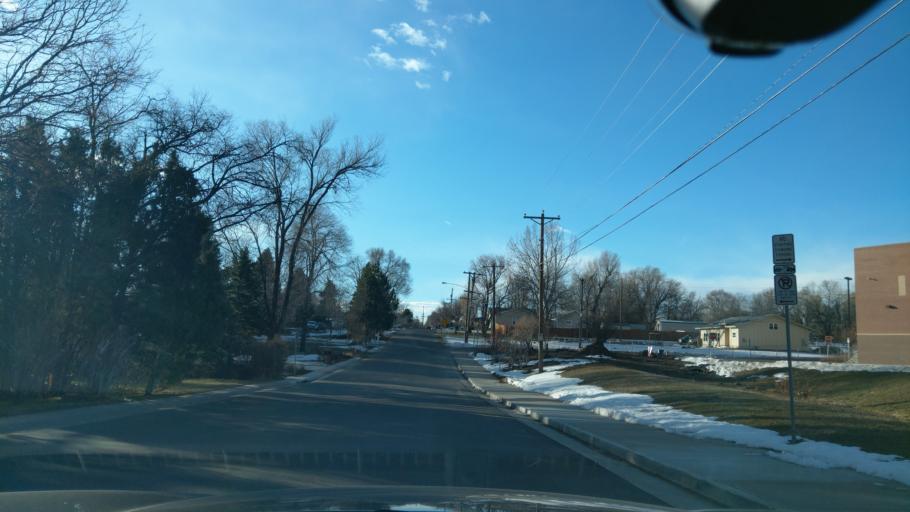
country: US
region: Colorado
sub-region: Jefferson County
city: Lakewood
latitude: 39.7285
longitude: -105.1050
